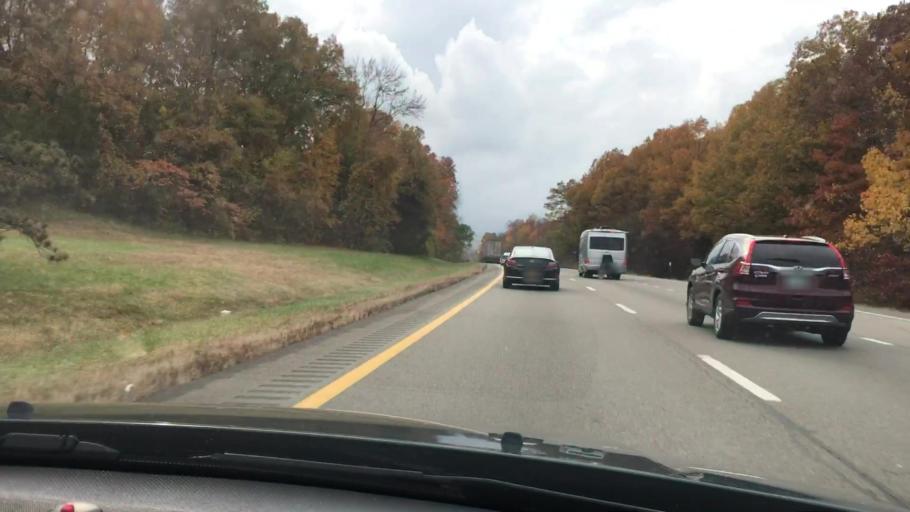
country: US
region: New York
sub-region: Dutchess County
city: Hillside Lake
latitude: 41.5381
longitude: -73.7784
